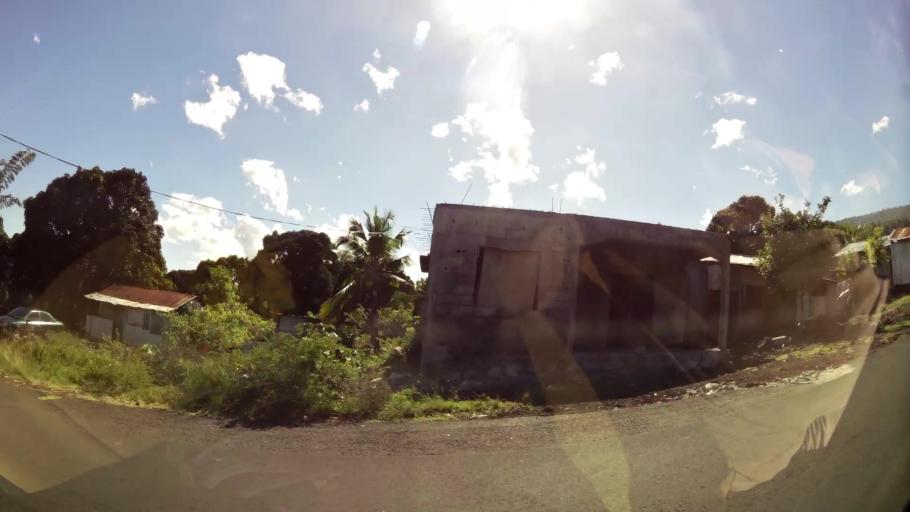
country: KM
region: Grande Comore
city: Tsidje
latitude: -11.6902
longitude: 43.2743
